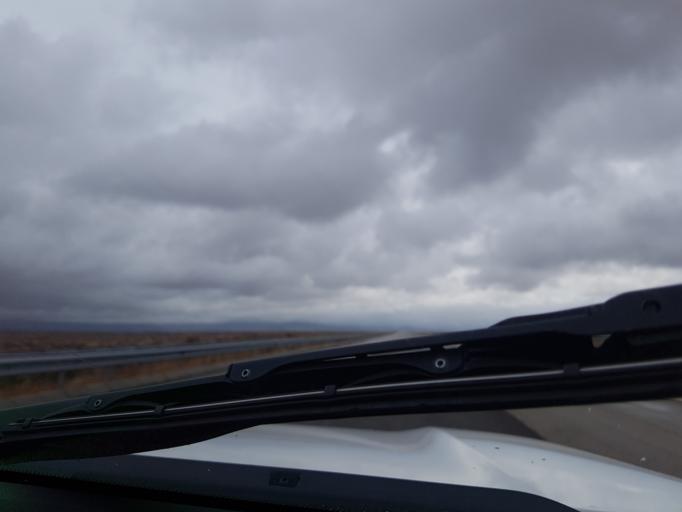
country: TM
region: Balkan
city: Balkanabat
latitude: 39.8507
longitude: 54.1008
